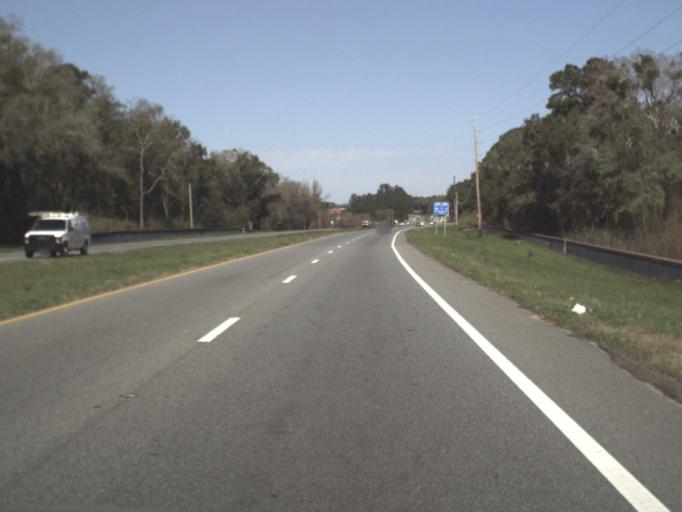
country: US
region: Florida
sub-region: Gadsden County
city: Midway
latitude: 30.5251
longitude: -84.3551
